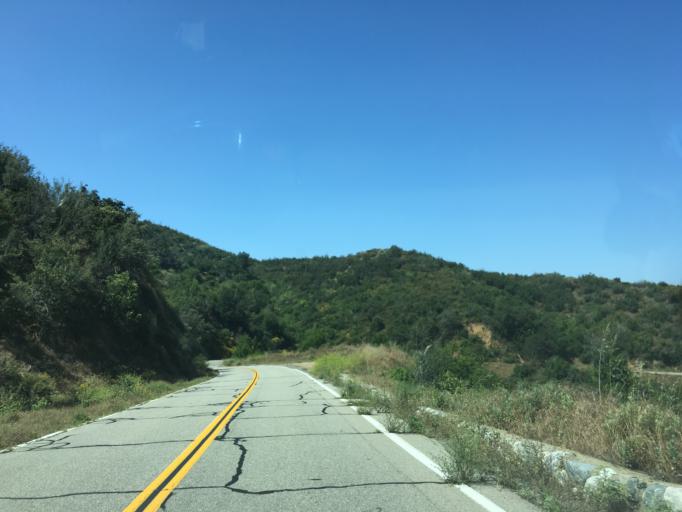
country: US
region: California
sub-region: Los Angeles County
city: Glendora
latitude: 34.1976
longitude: -117.8368
